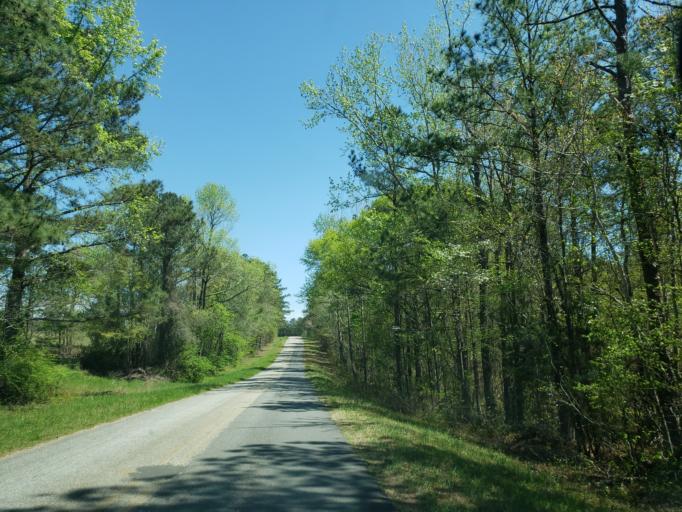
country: US
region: Alabama
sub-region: Tallapoosa County
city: Camp Hill
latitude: 32.6747
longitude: -85.7028
